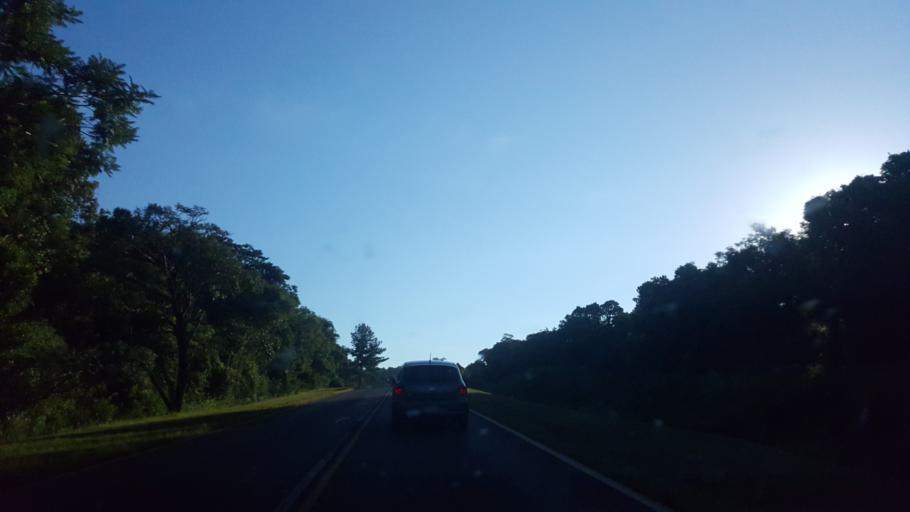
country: AR
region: Misiones
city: El Alcazar
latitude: -26.7205
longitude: -54.8593
